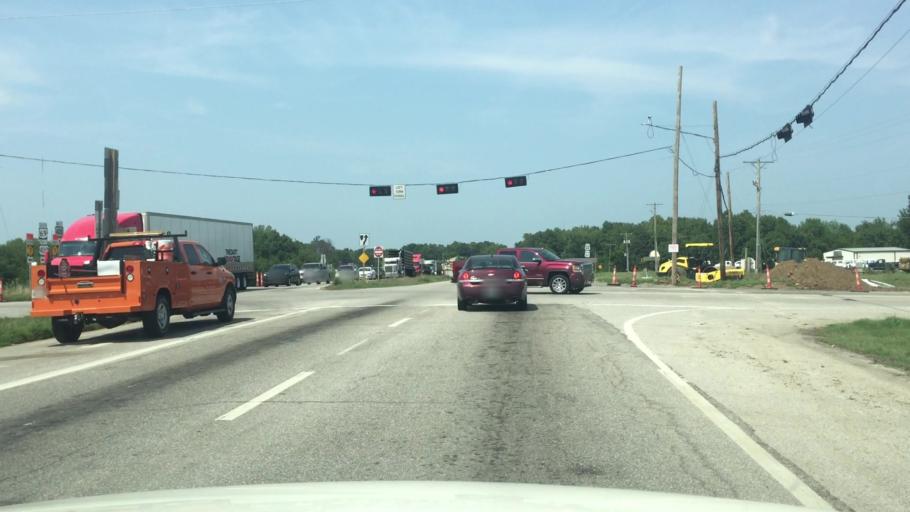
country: US
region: Kansas
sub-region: Crawford County
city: Pittsburg
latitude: 37.3383
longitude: -94.7053
